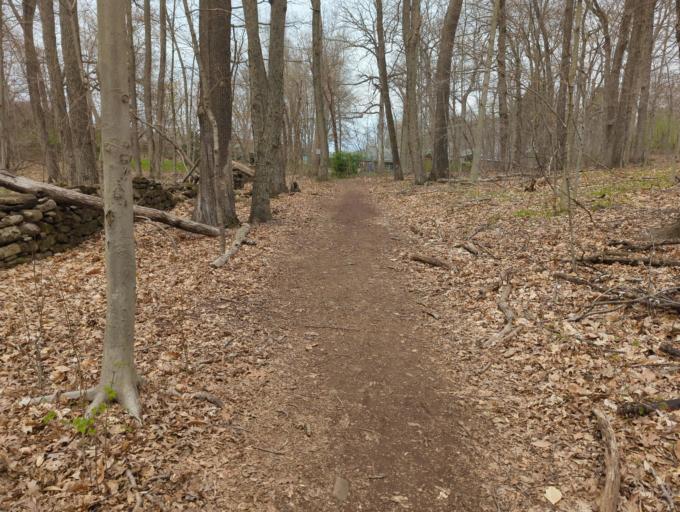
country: US
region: Connecticut
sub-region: Middlesex County
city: Middletown
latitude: 41.5388
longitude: -72.6727
